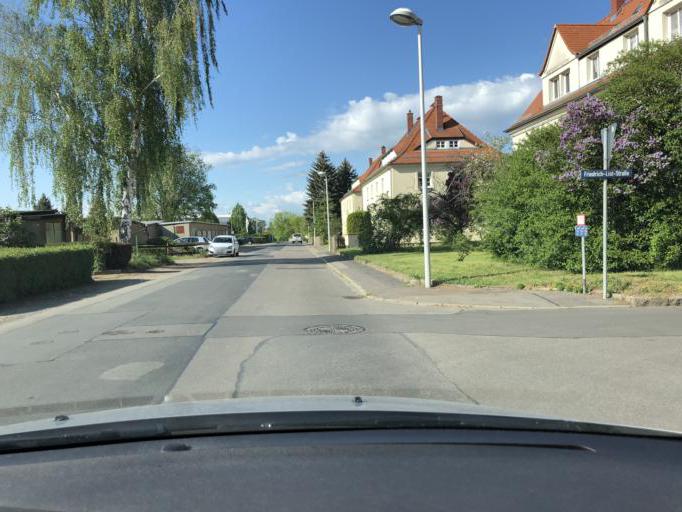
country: DE
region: Thuringia
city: Altenburg
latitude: 51.0095
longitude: 12.4388
